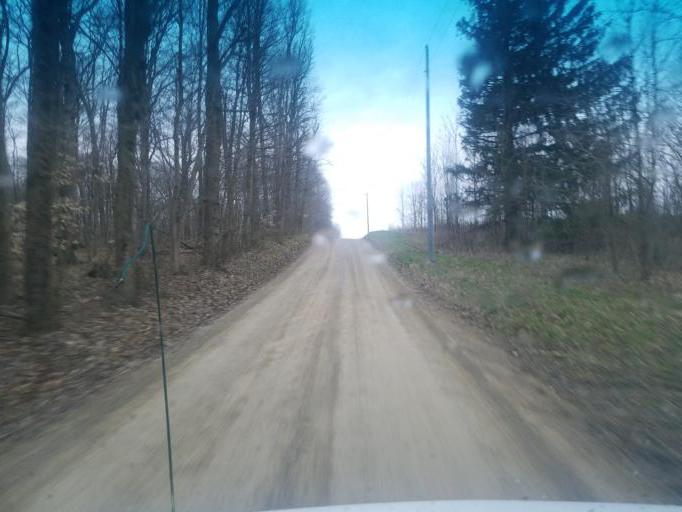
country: US
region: Ohio
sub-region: Knox County
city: Fredericktown
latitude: 40.5252
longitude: -82.4387
